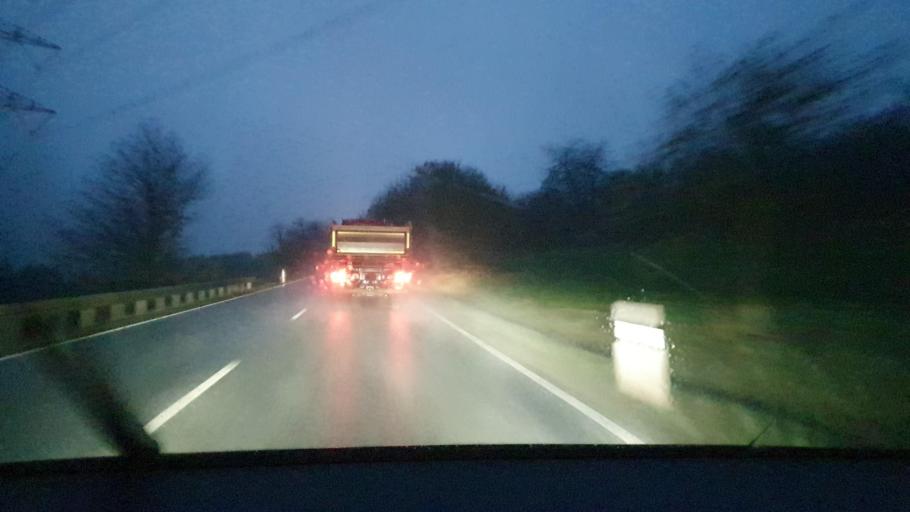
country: DE
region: Rheinland-Pfalz
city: Irmtraut
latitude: 50.5459
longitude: 8.0555
